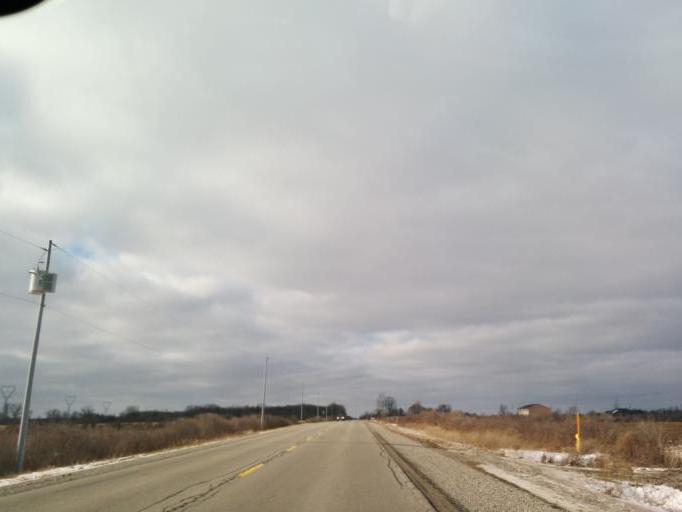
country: CA
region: Ontario
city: Brantford
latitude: 42.9809
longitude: -80.1027
